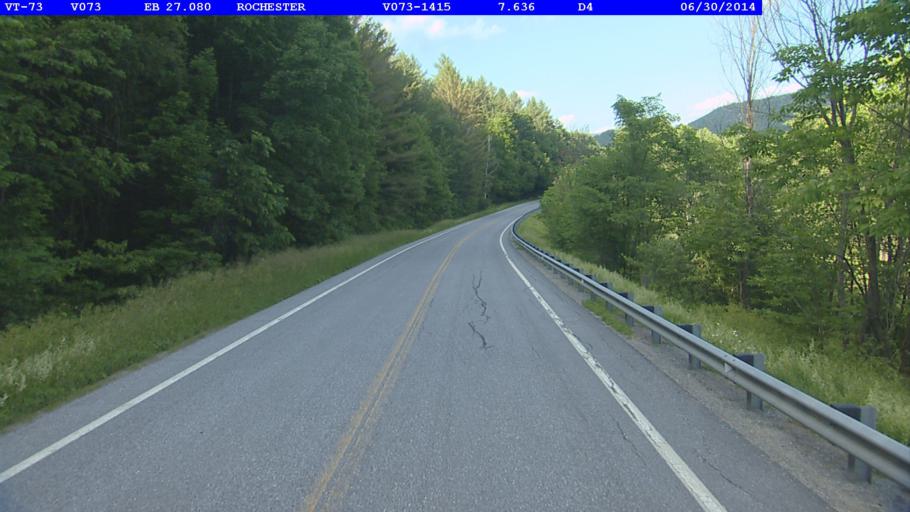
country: US
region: Vermont
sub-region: Orange County
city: Randolph
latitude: 43.8537
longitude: -72.8258
